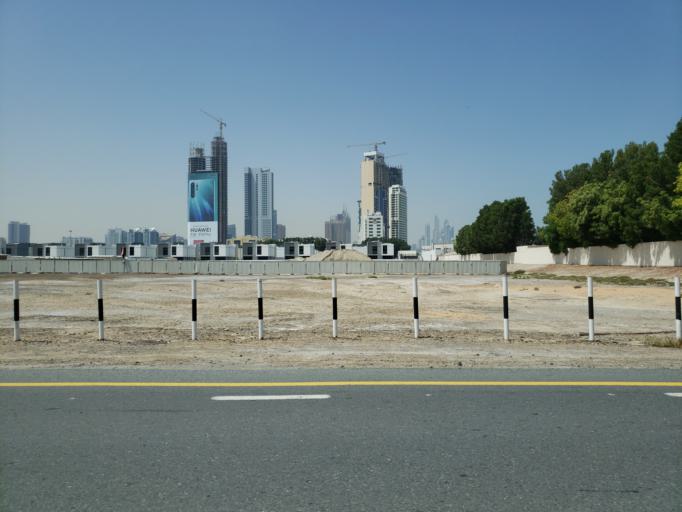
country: AE
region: Dubai
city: Dubai
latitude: 25.1162
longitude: 55.1839
